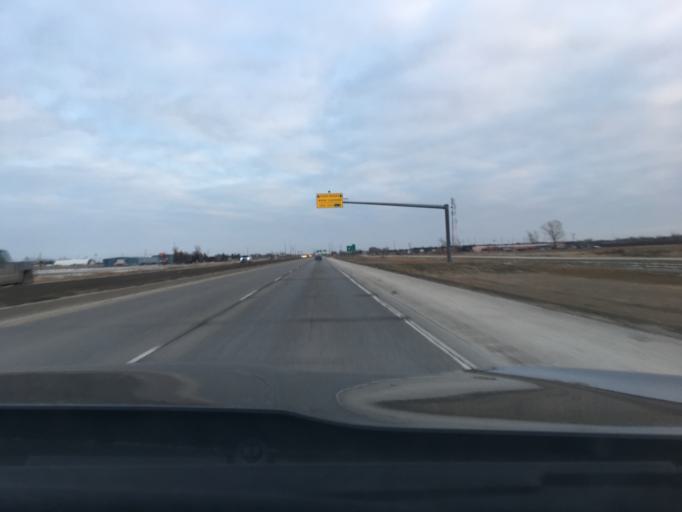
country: CA
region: Manitoba
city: Winnipeg
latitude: 49.9787
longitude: -97.0888
